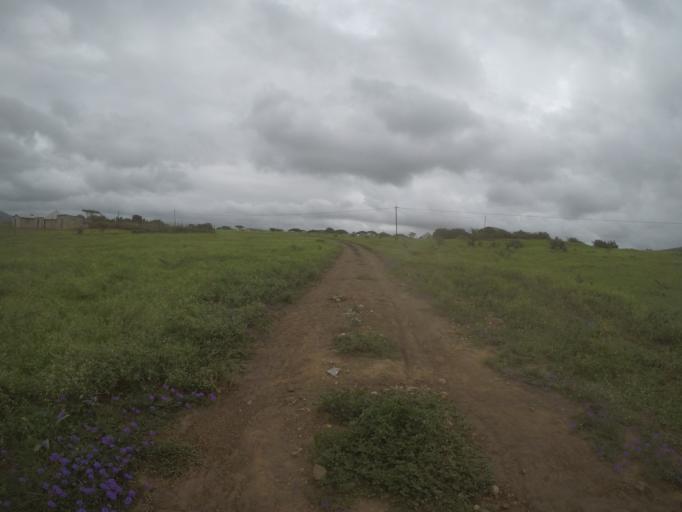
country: ZA
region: KwaZulu-Natal
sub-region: uThungulu District Municipality
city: Empangeni
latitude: -28.6078
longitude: 31.8701
